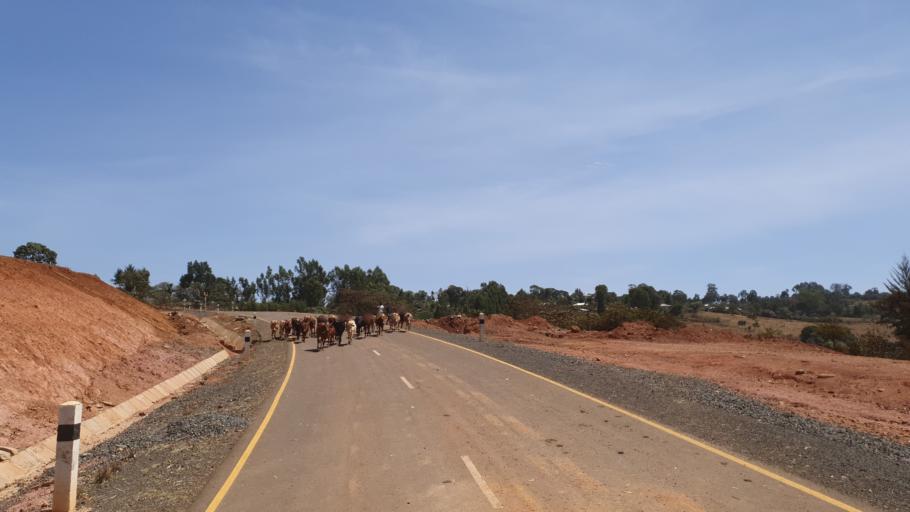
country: ET
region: Oromiya
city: Shambu
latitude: 9.8865
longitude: 36.6539
